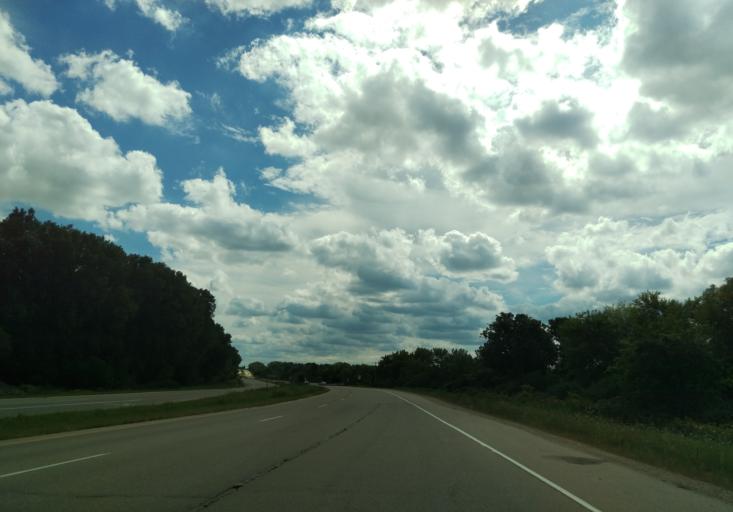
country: US
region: Wisconsin
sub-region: Dane County
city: Maple Bluff
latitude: 43.1531
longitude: -89.4039
